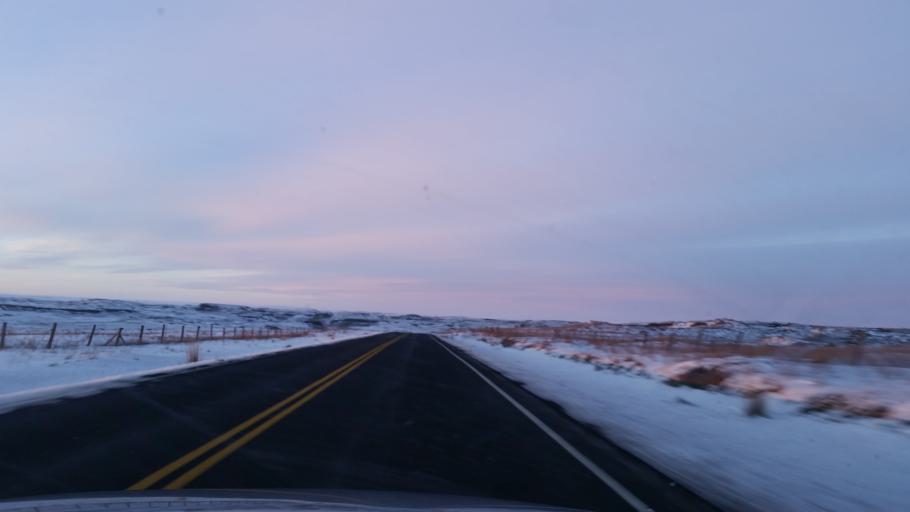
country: US
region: Washington
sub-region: Spokane County
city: Medical Lake
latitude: 47.2366
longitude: -117.9161
